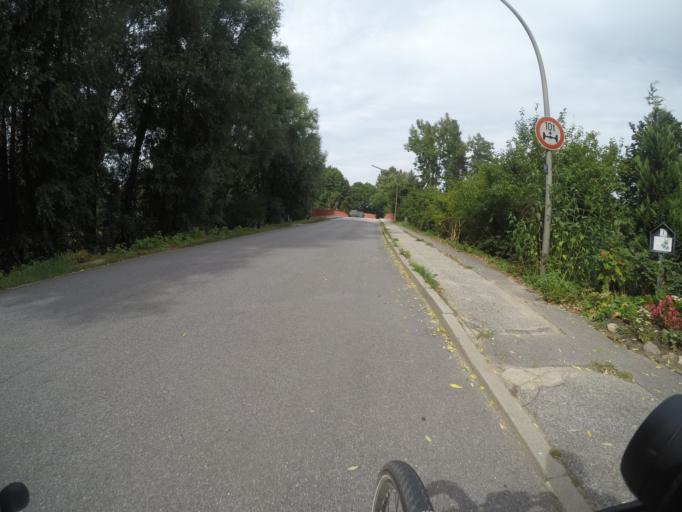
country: DE
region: Schleswig-Holstein
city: Oststeinbek
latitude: 53.4810
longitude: 10.1283
